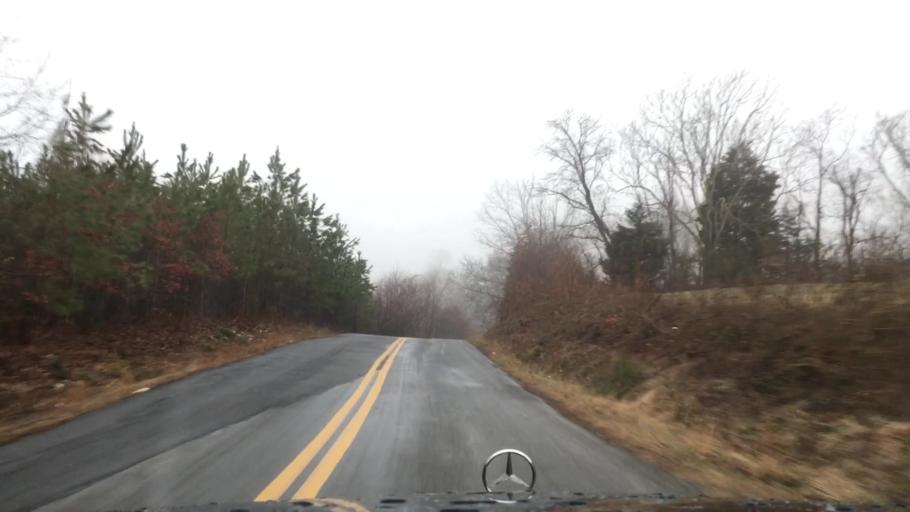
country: US
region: Virginia
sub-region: Pittsylvania County
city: Hurt
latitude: 37.1124
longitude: -79.3136
